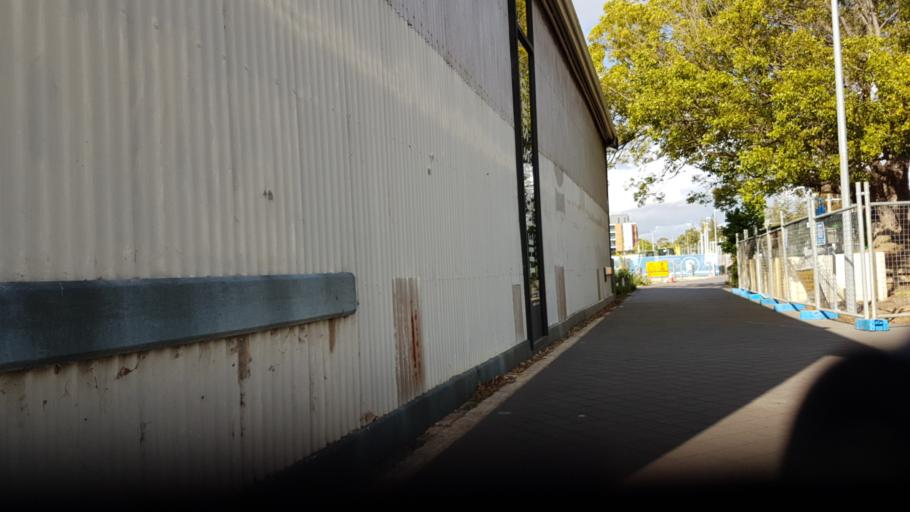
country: AU
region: Western Australia
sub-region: Claremont
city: Claremont
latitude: -31.9807
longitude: 115.7810
